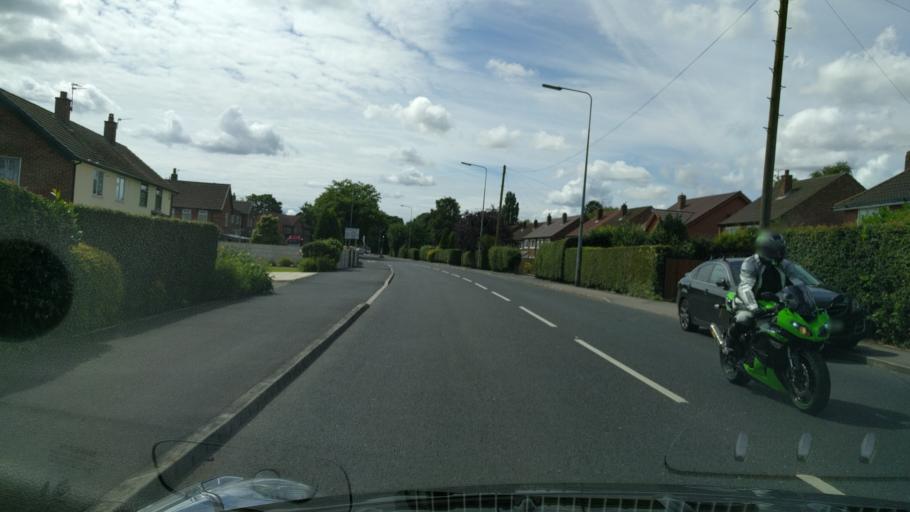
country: GB
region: England
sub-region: Warrington
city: Culcheth
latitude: 53.4531
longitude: -2.5149
